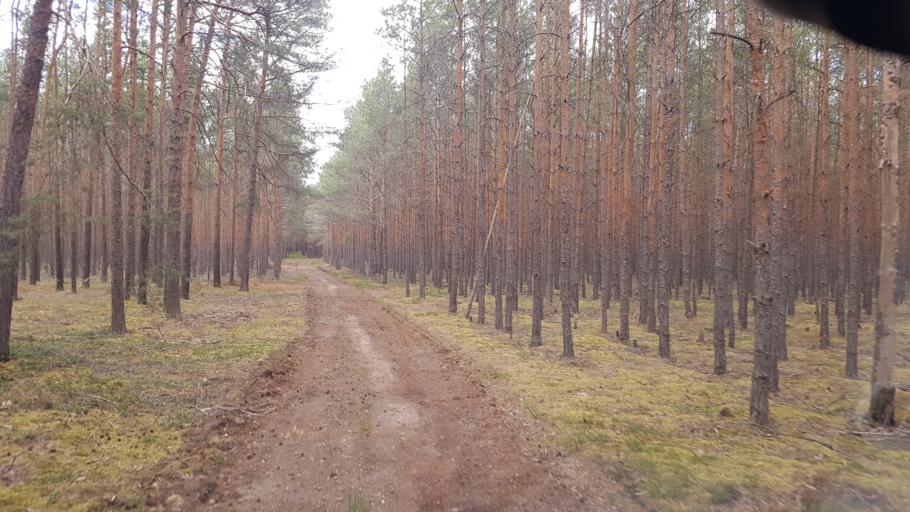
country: DE
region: Brandenburg
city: Finsterwalde
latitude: 51.6220
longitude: 13.6579
